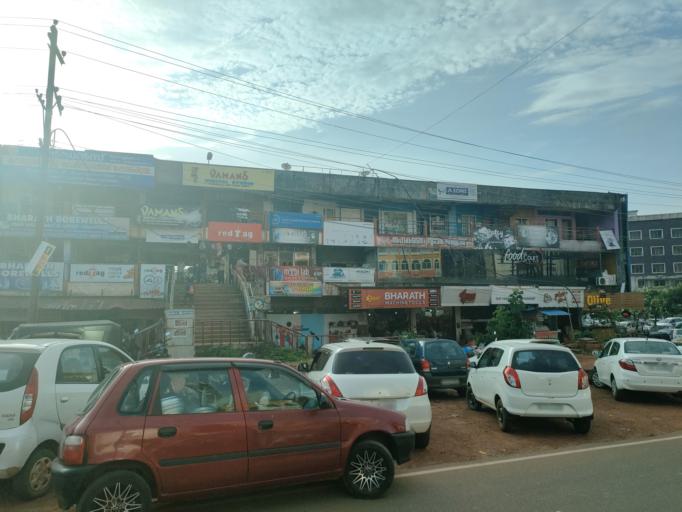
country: IN
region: Kerala
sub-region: Kasaragod District
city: Kasaragod
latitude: 12.5073
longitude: 74.9950
